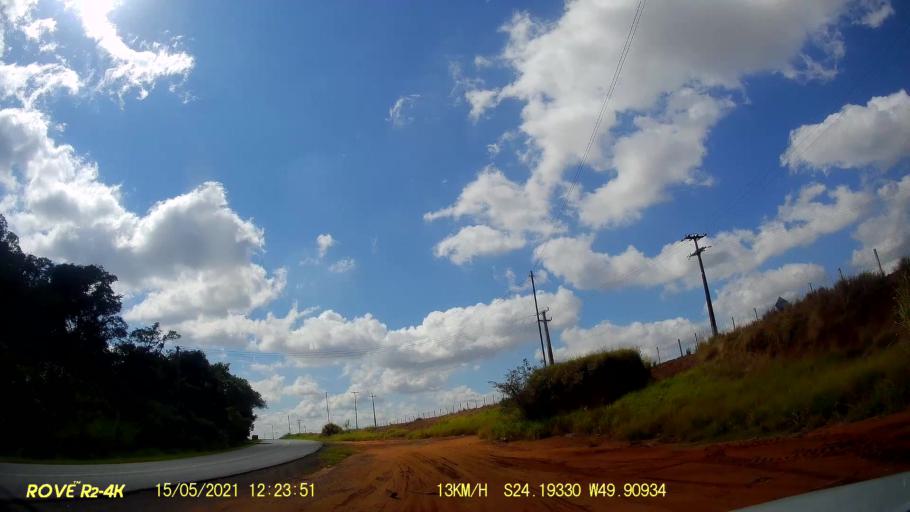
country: BR
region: Parana
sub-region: Jaguariaiva
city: Jaguariaiva
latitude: -24.1934
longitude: -49.9096
